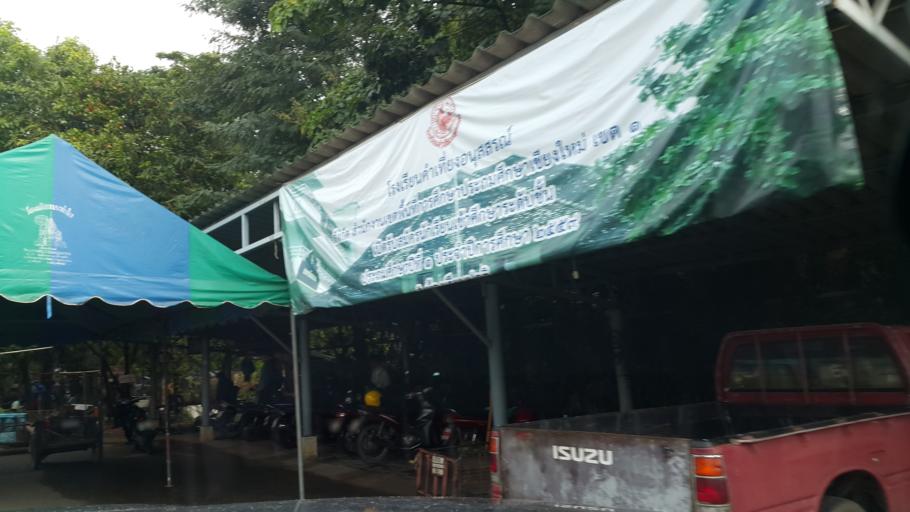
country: TH
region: Chiang Mai
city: Chiang Mai
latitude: 18.8063
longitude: 98.9972
